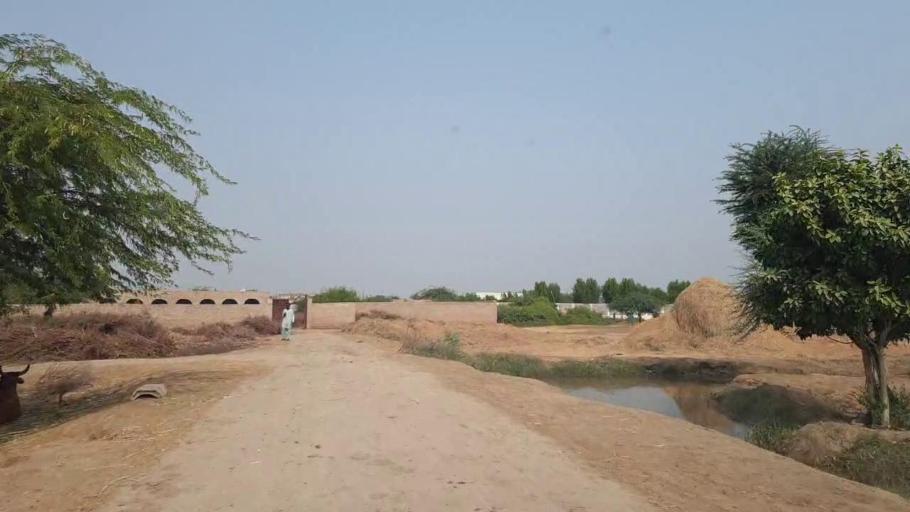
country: PK
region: Sindh
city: Matli
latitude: 25.1518
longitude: 68.7021
